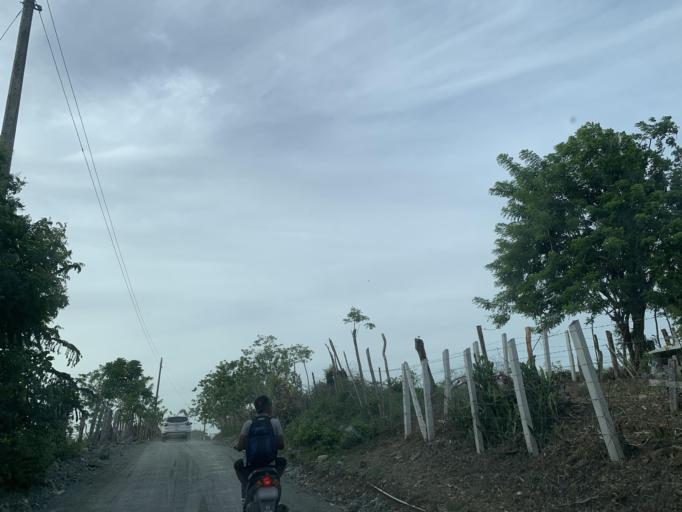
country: DO
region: Santiago
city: Pedro Garcia
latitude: 19.6988
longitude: -70.6142
